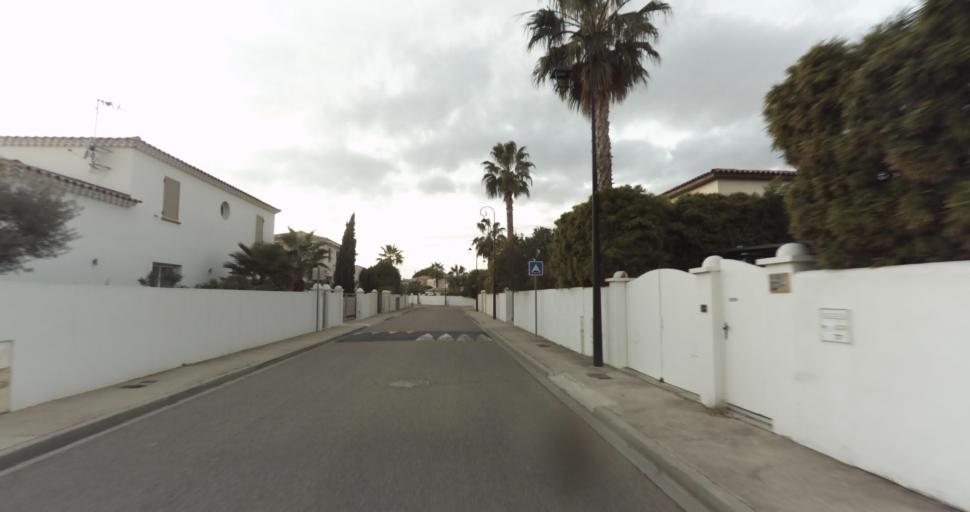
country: FR
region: Languedoc-Roussillon
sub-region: Departement du Gard
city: Aigues-Mortes
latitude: 43.5764
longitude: 4.1897
